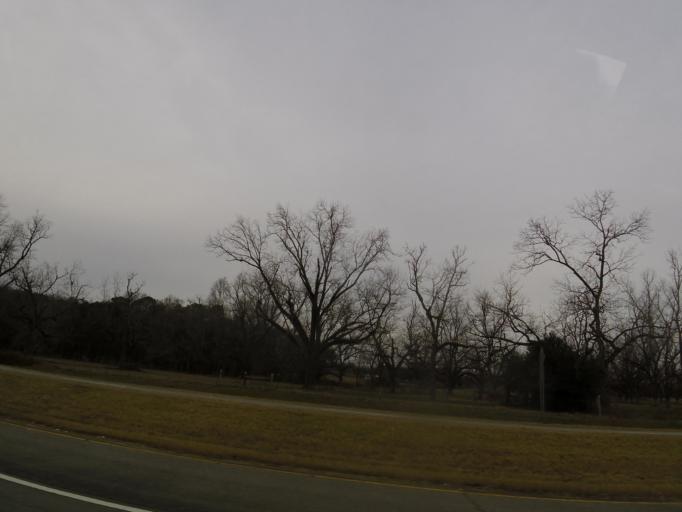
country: US
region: Georgia
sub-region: Grady County
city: Cairo
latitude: 30.8694
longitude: -84.0993
